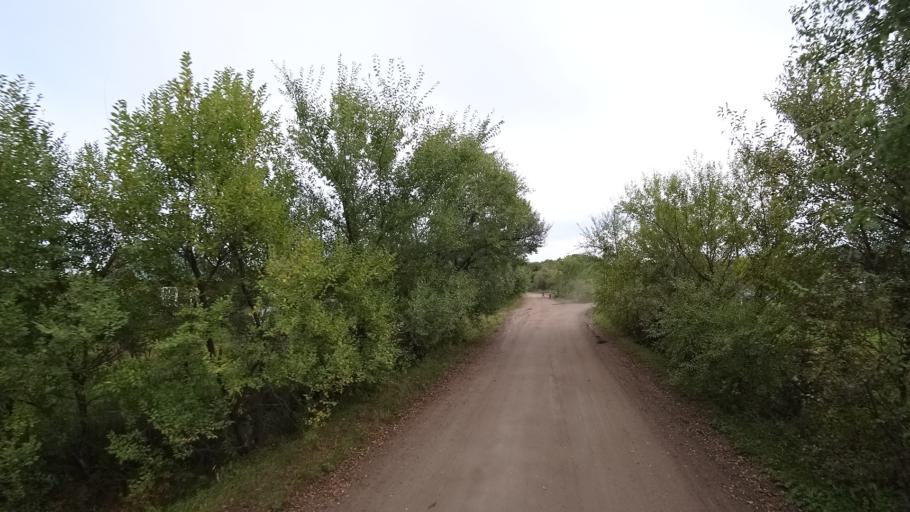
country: RU
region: Amur
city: Arkhara
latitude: 49.3524
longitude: 130.1104
